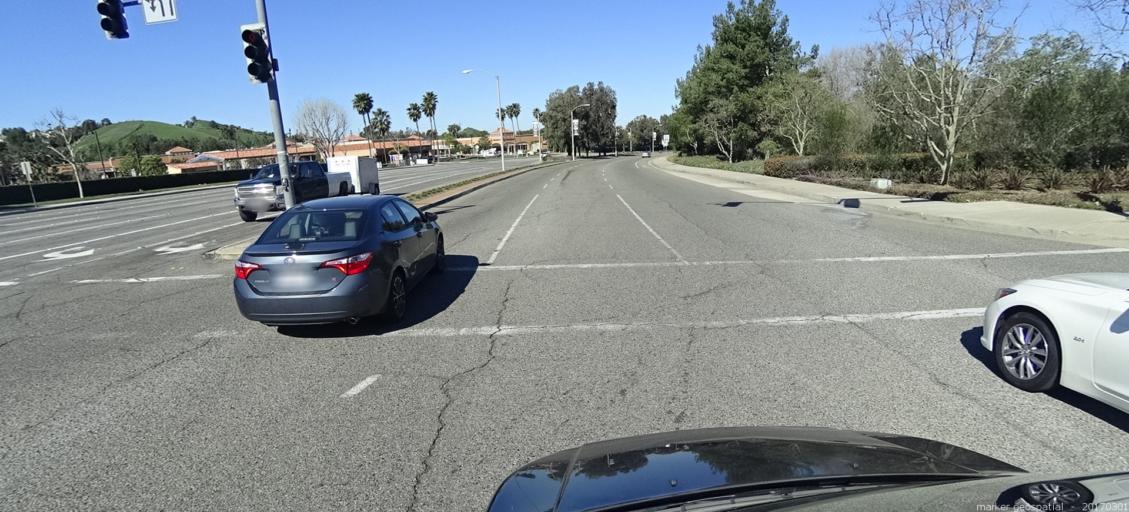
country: US
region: California
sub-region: Orange County
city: Yorba Linda
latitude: 33.8618
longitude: -117.7369
